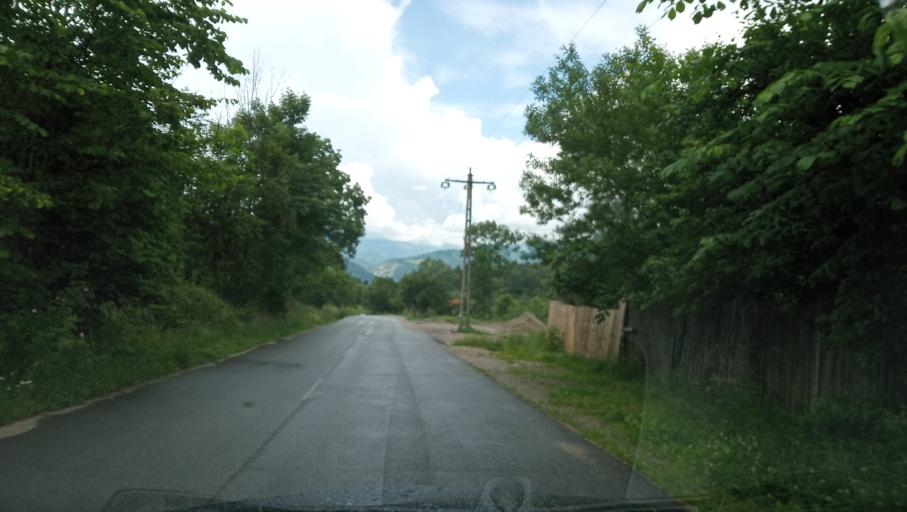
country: RO
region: Hunedoara
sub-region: Oras Petrila
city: Petrila
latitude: 45.4113
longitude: 23.4118
